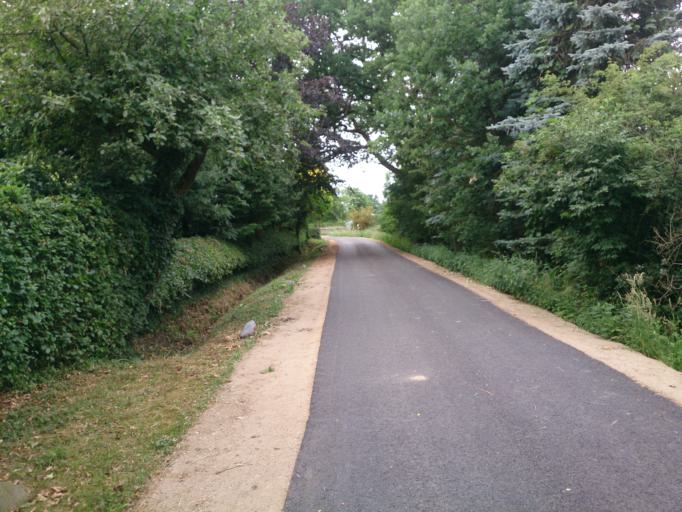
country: DE
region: Schleswig-Holstein
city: Bevern
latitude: 53.7386
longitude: 9.8049
